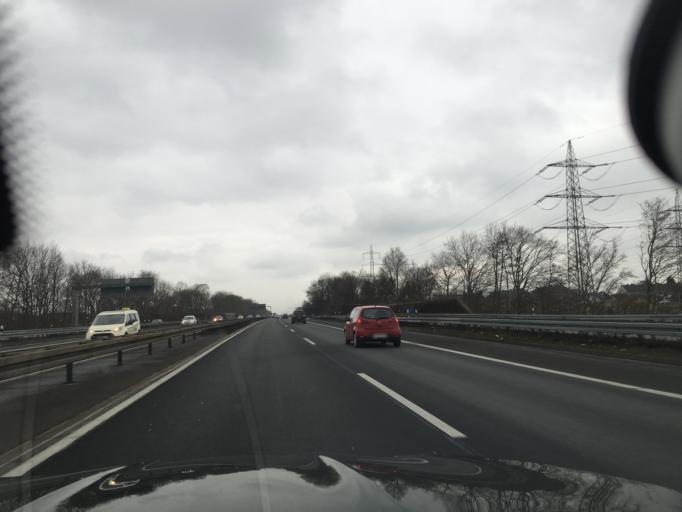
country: DE
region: North Rhine-Westphalia
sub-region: Regierungsbezirk Koln
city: Eil
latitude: 50.8842
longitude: 7.0940
